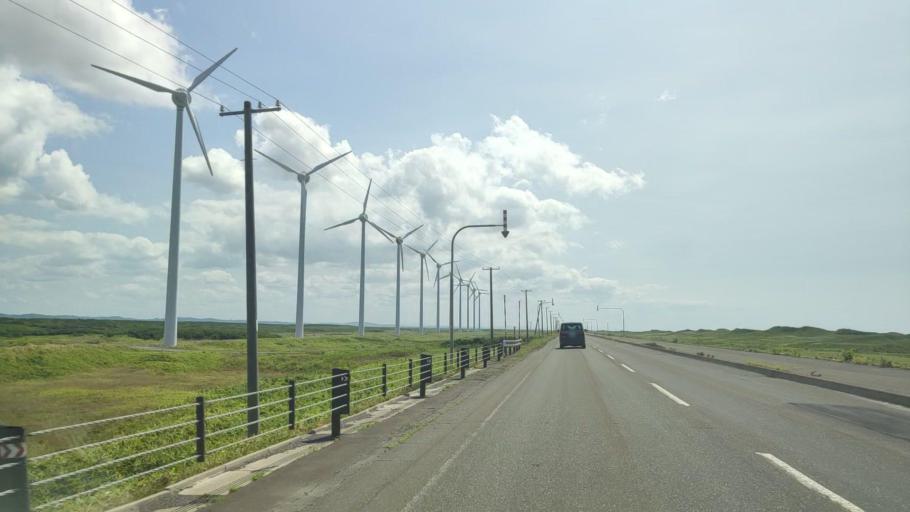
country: JP
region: Hokkaido
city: Makubetsu
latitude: 44.9684
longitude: 141.7007
